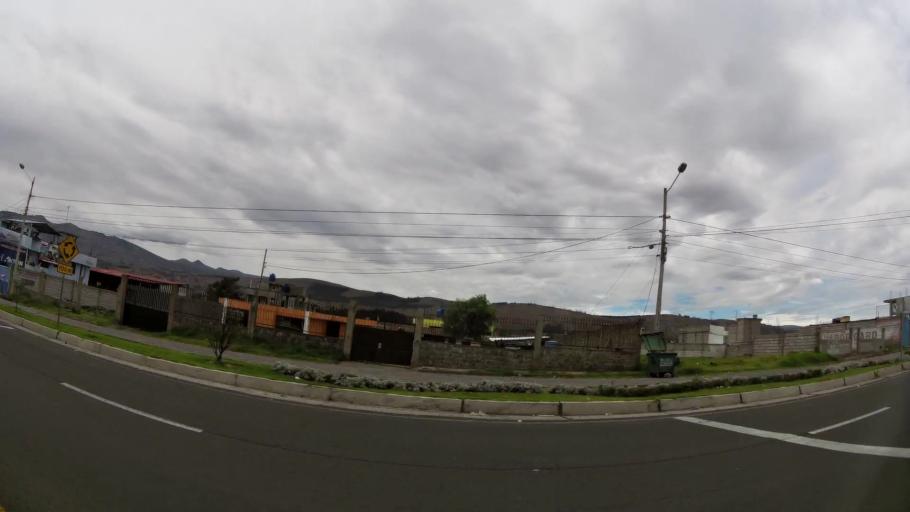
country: EC
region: Cotopaxi
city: San Miguel de Salcedo
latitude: -1.0293
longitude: -78.5910
